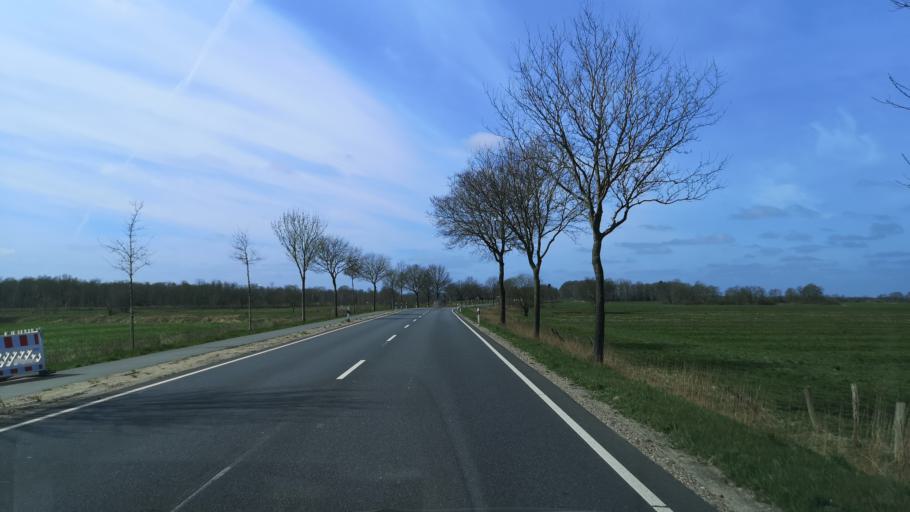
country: DE
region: Schleswig-Holstein
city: Prinzenmoor
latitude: 54.2221
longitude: 9.4675
